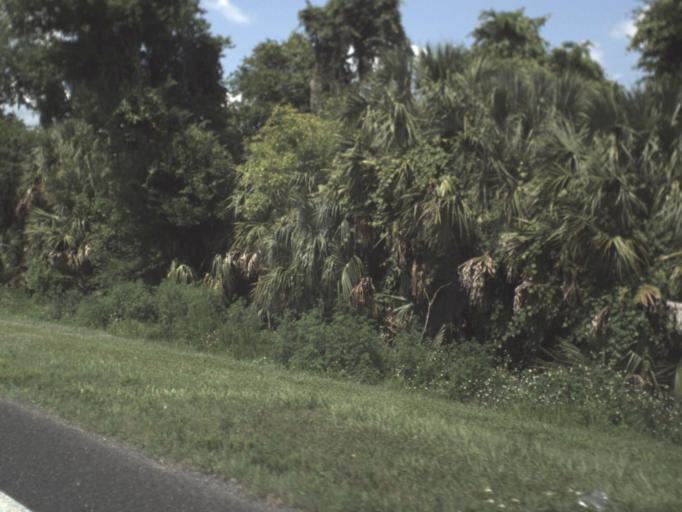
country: US
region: Florida
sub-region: Marion County
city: Citra
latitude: 29.4400
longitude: -82.1091
